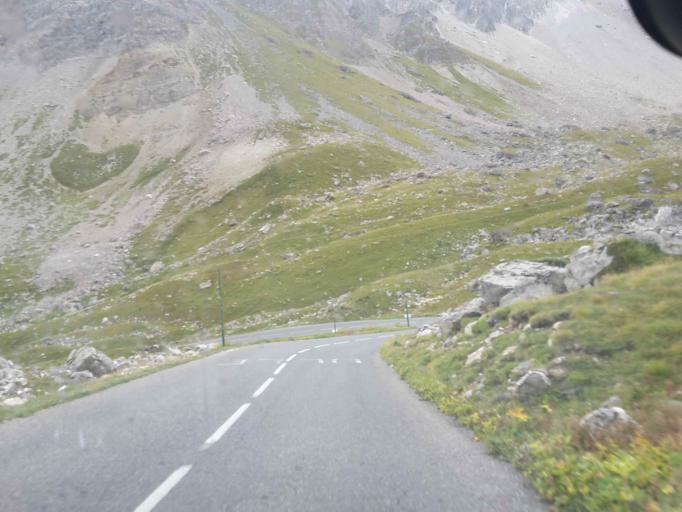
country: FR
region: Rhone-Alpes
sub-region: Departement de la Savoie
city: Valloire
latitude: 45.0785
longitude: 6.4240
